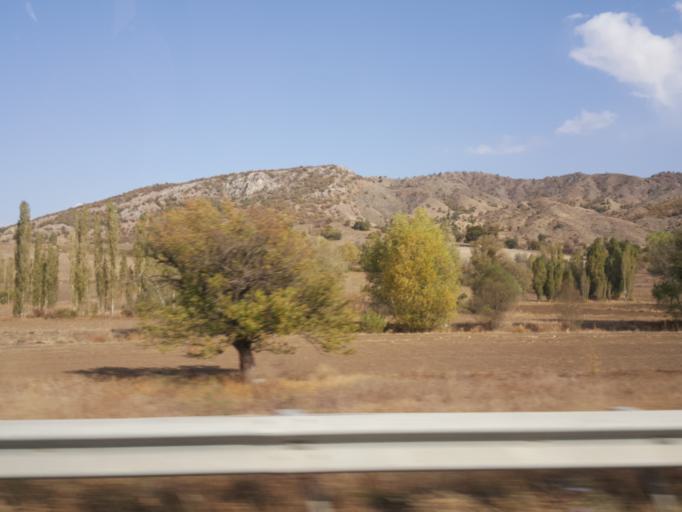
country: TR
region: Corum
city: Seydim
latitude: 40.3729
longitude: 34.7277
